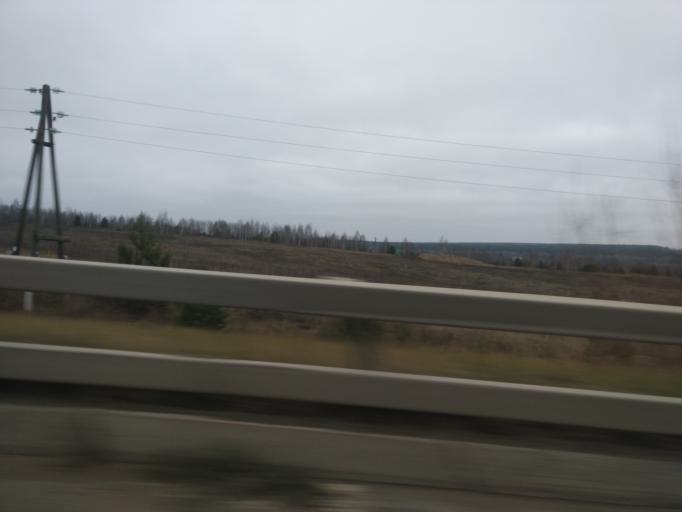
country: RU
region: Kirov
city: Krasnaya Polyana
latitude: 56.2310
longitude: 51.2153
